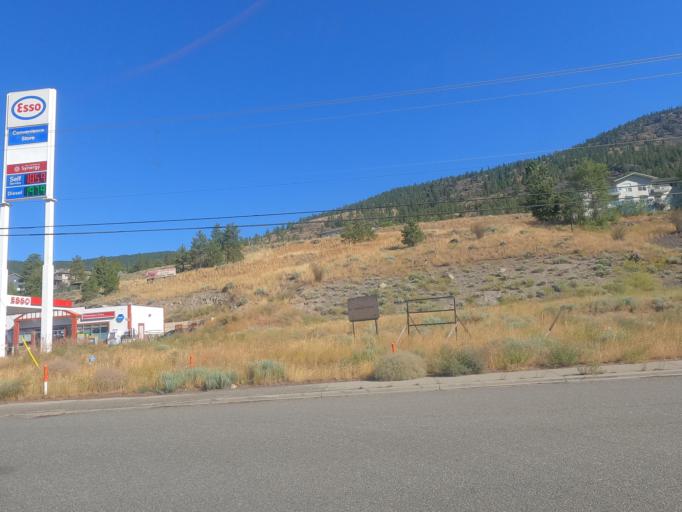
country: CA
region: British Columbia
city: Merritt
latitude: 50.1238
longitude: -120.7598
